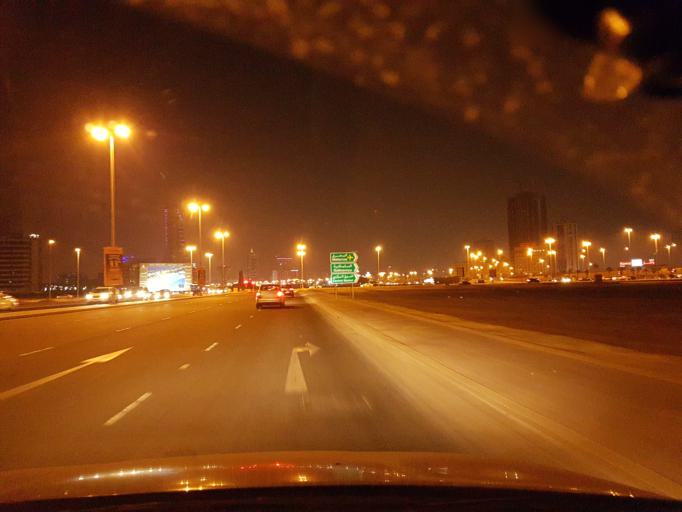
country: BH
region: Manama
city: Jidd Hafs
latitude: 26.2349
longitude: 50.5587
